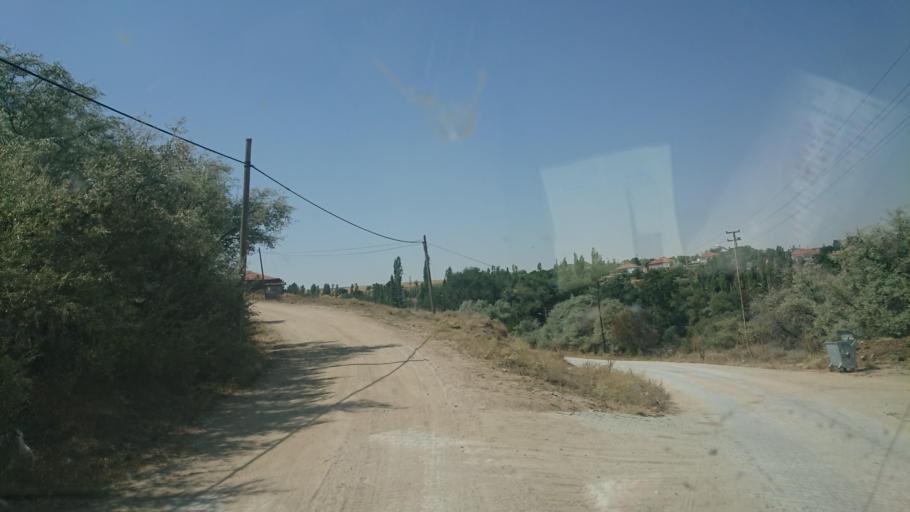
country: TR
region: Aksaray
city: Agacoren
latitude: 38.8181
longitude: 33.9548
